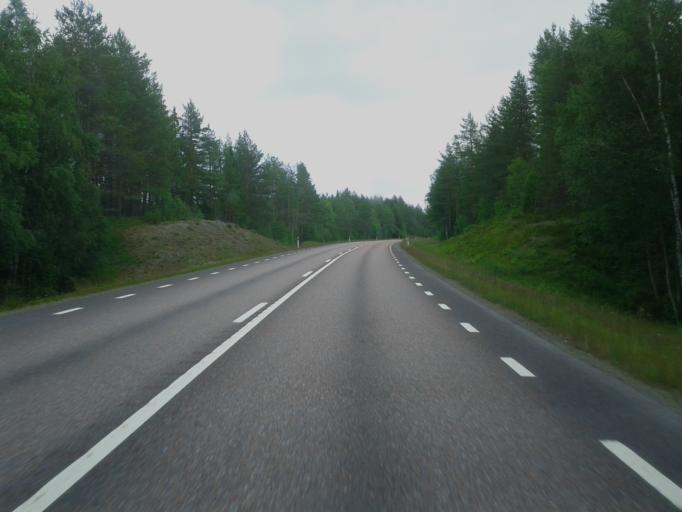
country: SE
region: Vaesterbotten
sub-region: Skelleftea Kommun
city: Burea
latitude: 64.3323
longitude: 21.2060
